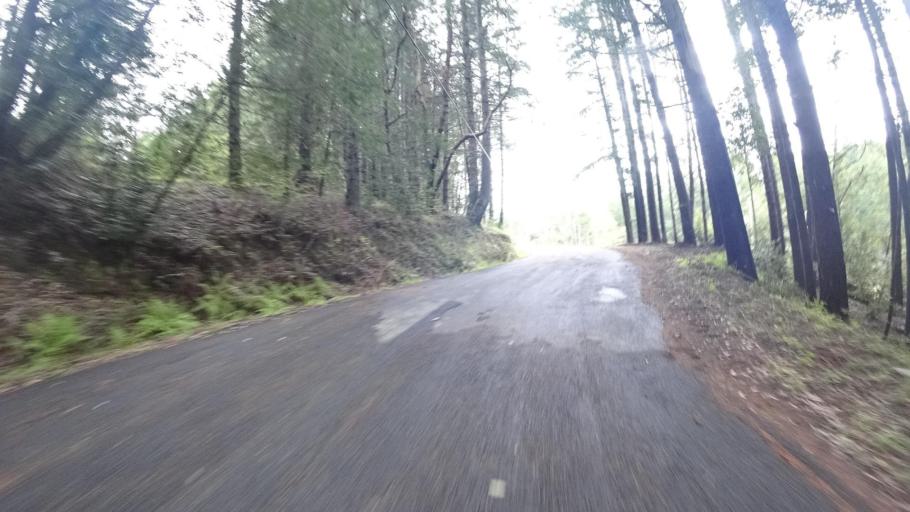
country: US
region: California
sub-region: Humboldt County
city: Blue Lake
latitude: 40.8634
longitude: -123.9104
